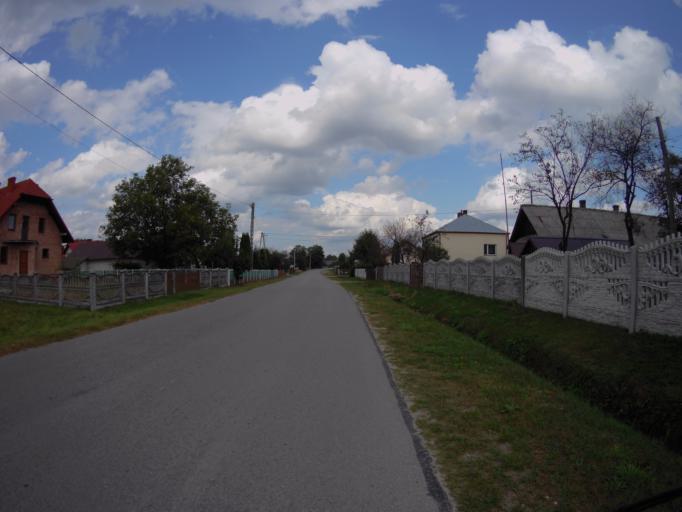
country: PL
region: Subcarpathian Voivodeship
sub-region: Powiat lezajski
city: Brzoza Krolewska
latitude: 50.2391
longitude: 22.3275
